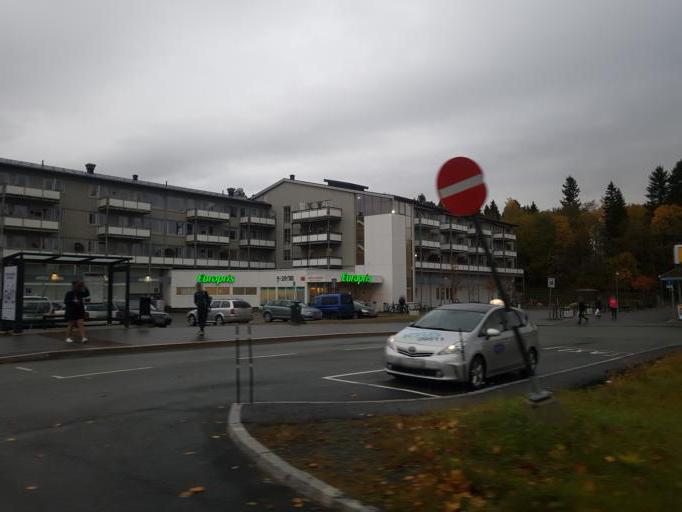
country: NO
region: Sor-Trondelag
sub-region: Trondheim
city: Trondheim
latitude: 63.3733
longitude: 10.3458
